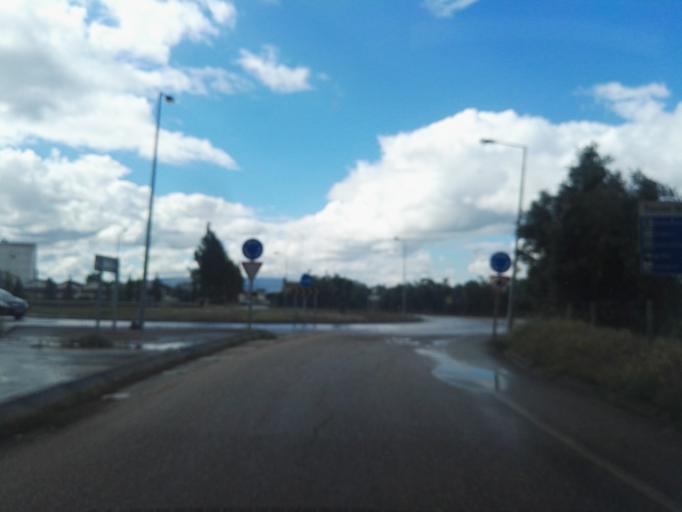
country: PT
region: Santarem
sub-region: Torres Novas
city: Riachos
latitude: 39.4296
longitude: -8.5042
